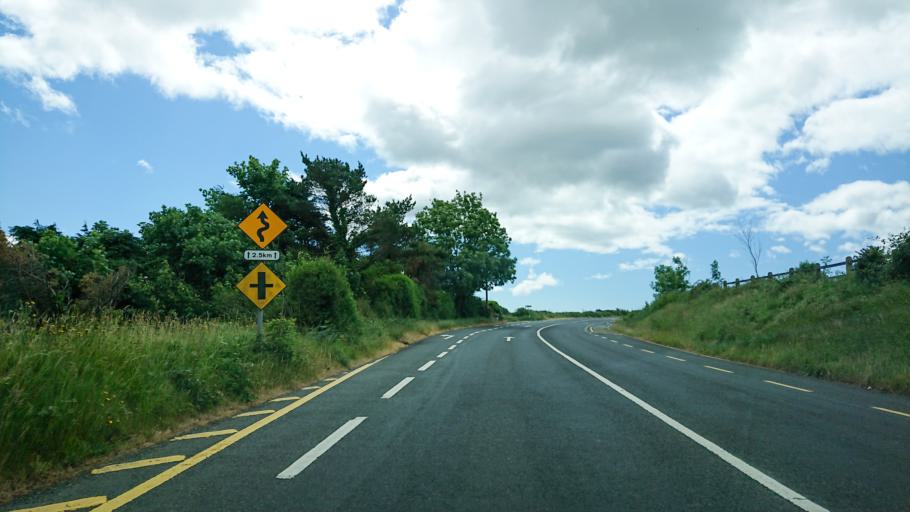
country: IE
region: Munster
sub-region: Waterford
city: Tra Mhor
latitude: 52.2140
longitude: -7.1948
